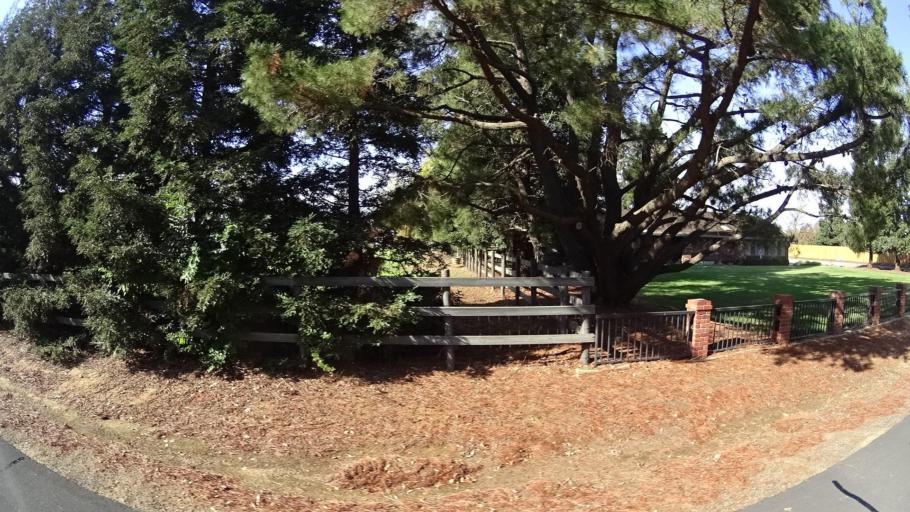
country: US
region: California
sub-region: Sacramento County
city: Wilton
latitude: 38.4370
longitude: -121.2883
